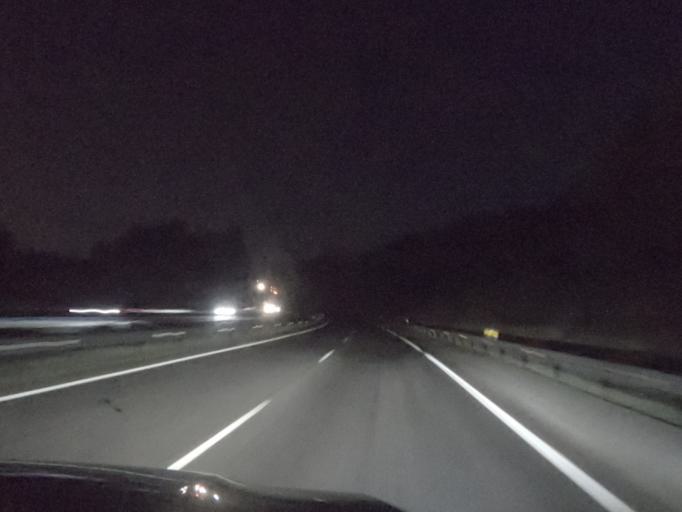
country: ES
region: Galicia
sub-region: Provincia de Ourense
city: Ourense
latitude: 42.3342
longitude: -7.8866
